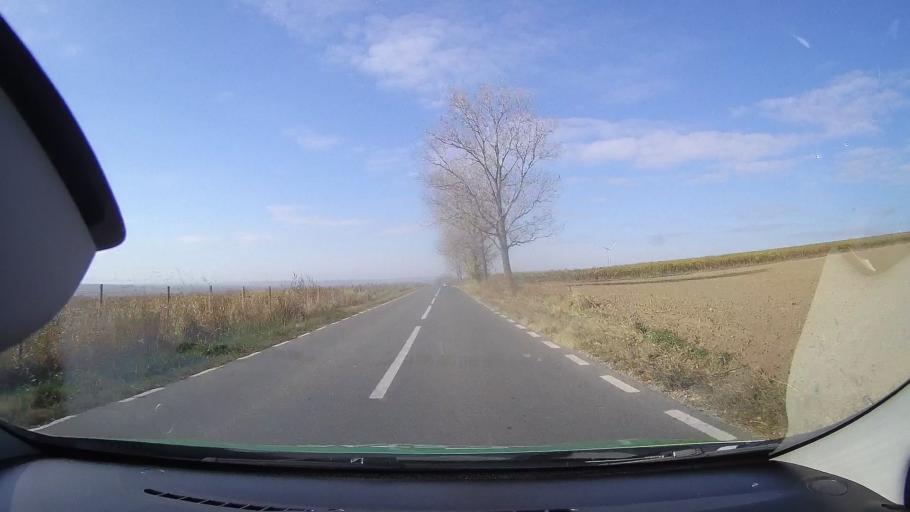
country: RO
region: Tulcea
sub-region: Comuna Valea Nucarilor
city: Iazurile
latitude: 45.0249
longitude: 28.9828
